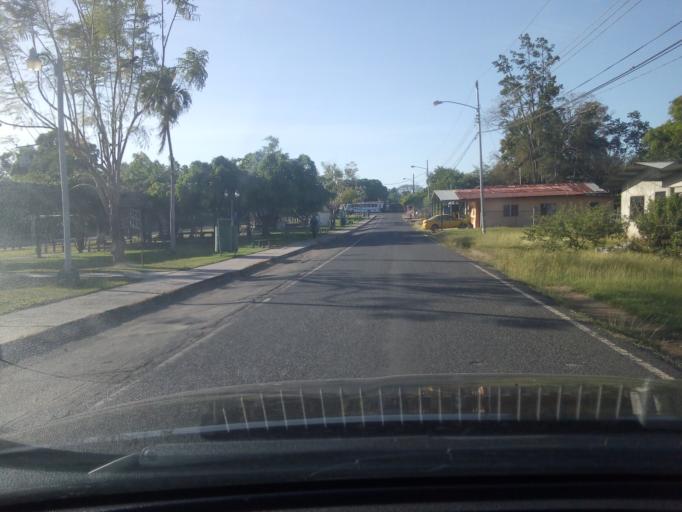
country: PA
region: Veraguas
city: Atalaya
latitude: 8.0436
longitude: -80.9246
